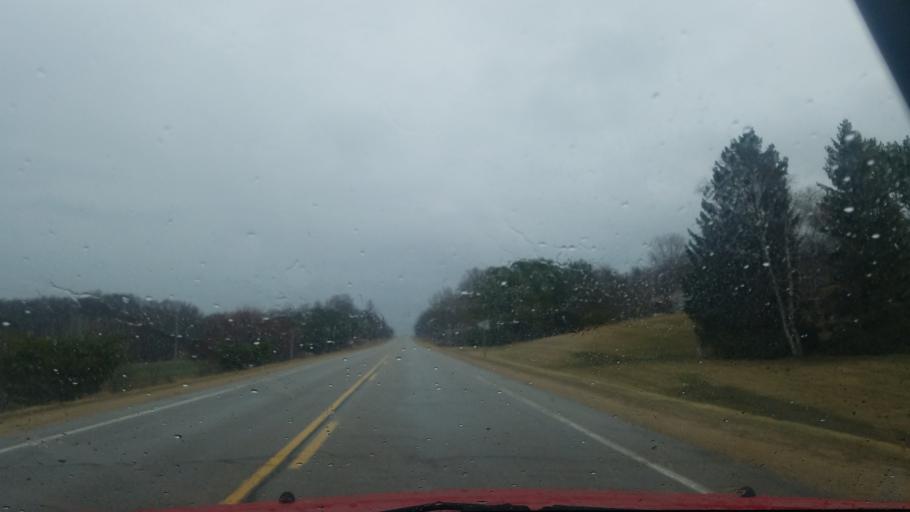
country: US
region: Wisconsin
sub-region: Dunn County
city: Menomonie
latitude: 44.9376
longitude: -91.9219
